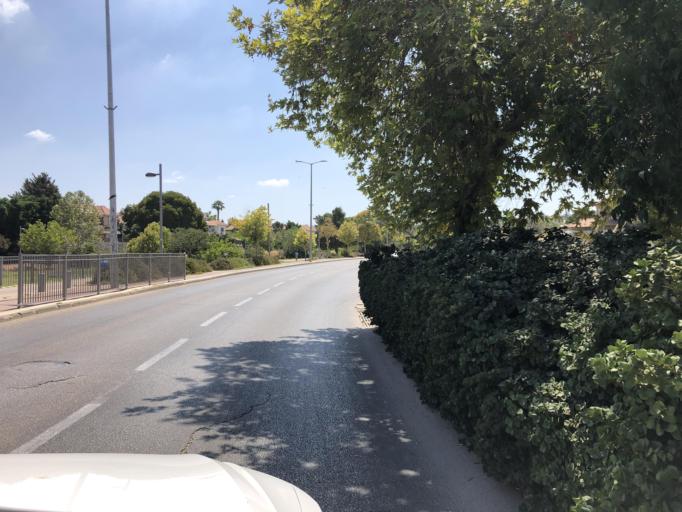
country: IL
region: Central District
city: Rosh Ha'Ayin
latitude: 32.1004
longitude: 34.9558
